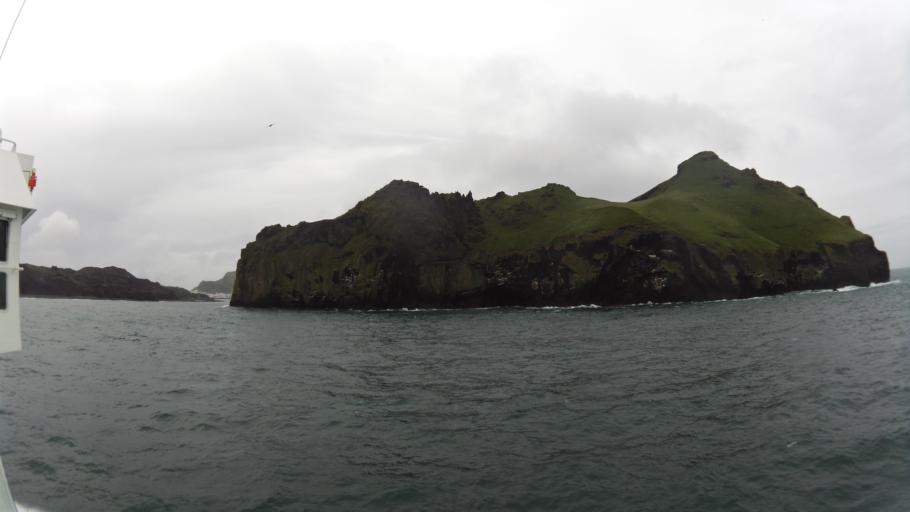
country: IS
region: South
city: Vestmannaeyjar
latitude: 63.4494
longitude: -20.2379
